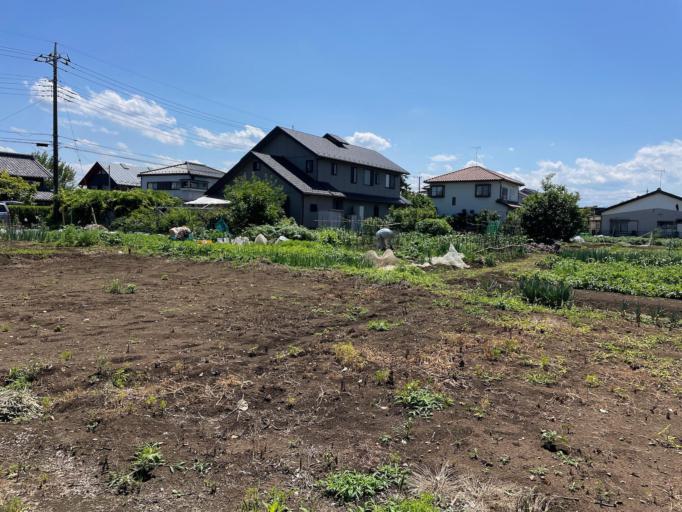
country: JP
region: Saitama
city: Sakado
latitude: 36.0009
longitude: 139.4144
